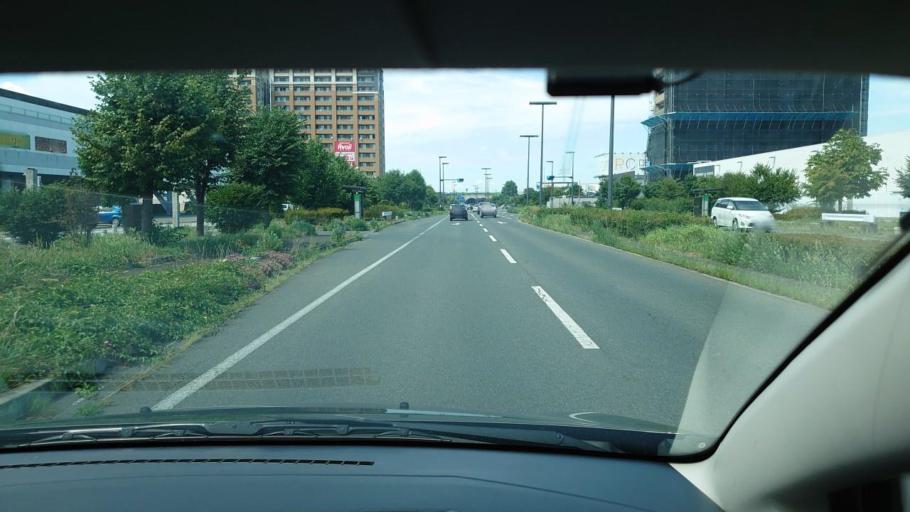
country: JP
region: Iwate
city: Morioka-shi
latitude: 39.6858
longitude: 141.1265
